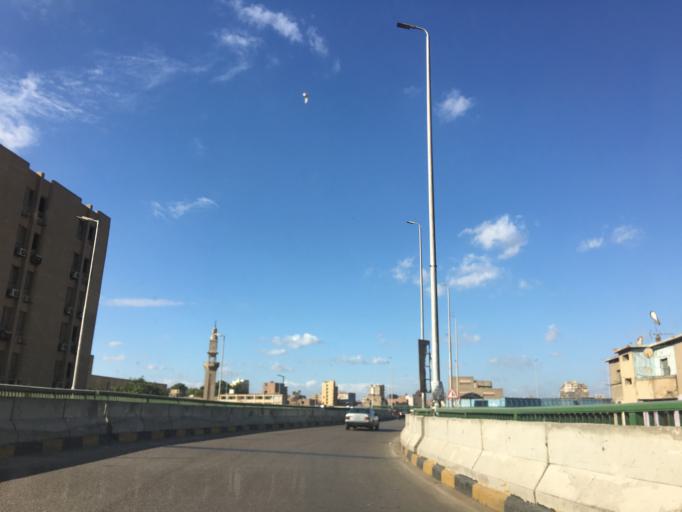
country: EG
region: Al Jizah
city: Al Jizah
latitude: 30.0277
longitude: 31.2003
